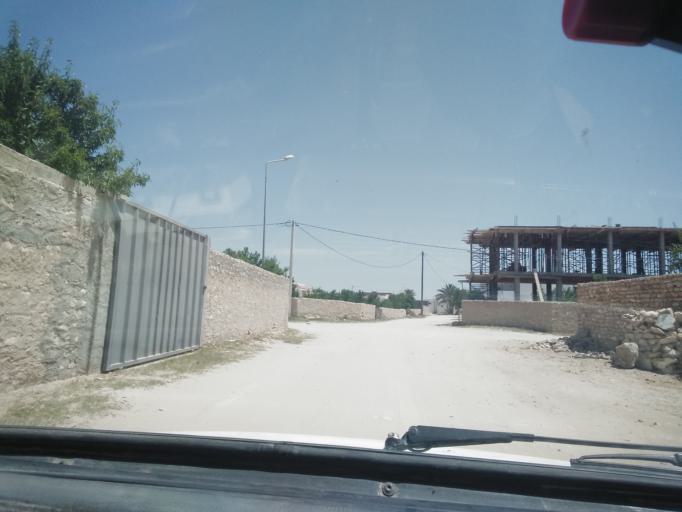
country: TN
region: Safaqis
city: Al Qarmadah
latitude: 34.8080
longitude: 10.7726
